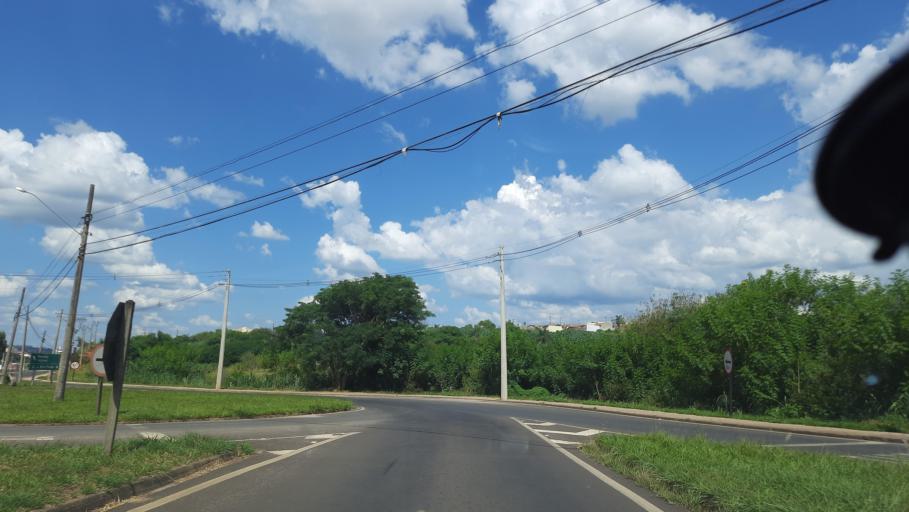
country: BR
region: Sao Paulo
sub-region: Sao Jose Do Rio Pardo
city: Sao Jose do Rio Pardo
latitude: -21.6036
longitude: -46.9157
